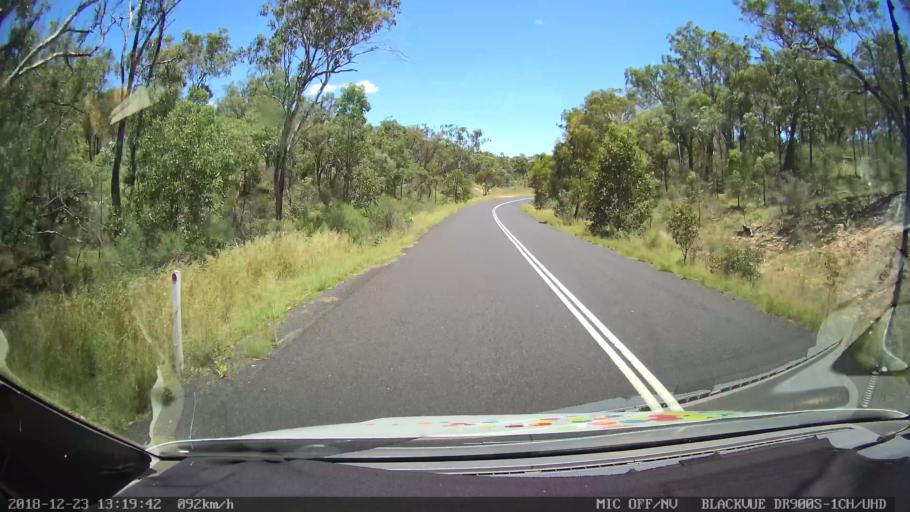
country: AU
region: New South Wales
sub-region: Armidale Dumaresq
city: Armidale
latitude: -30.4853
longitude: 151.4607
